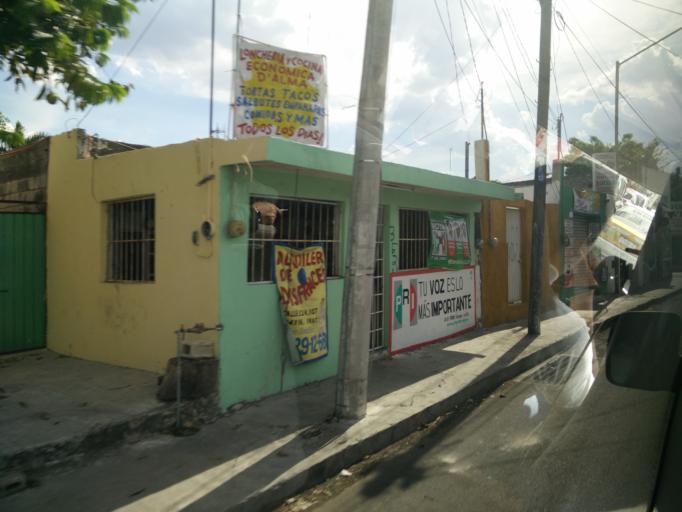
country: MX
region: Yucatan
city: Merida
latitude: 20.9647
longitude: -89.6048
